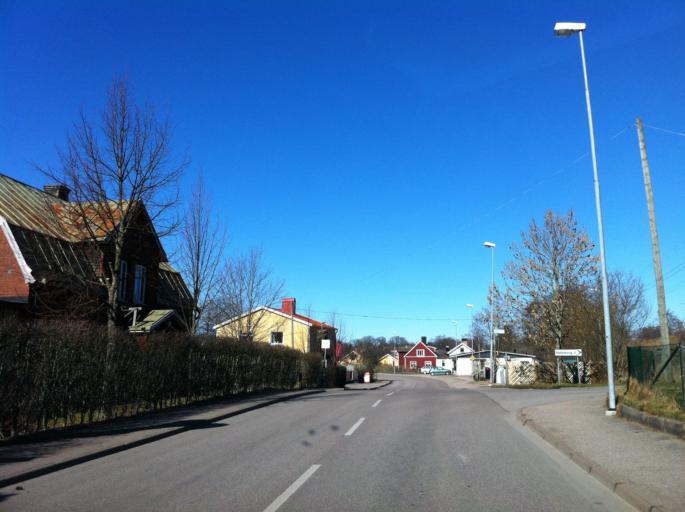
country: SE
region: Vaestra Goetaland
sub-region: Vanersborgs Kommun
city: Vargon
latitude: 58.3509
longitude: 12.4103
